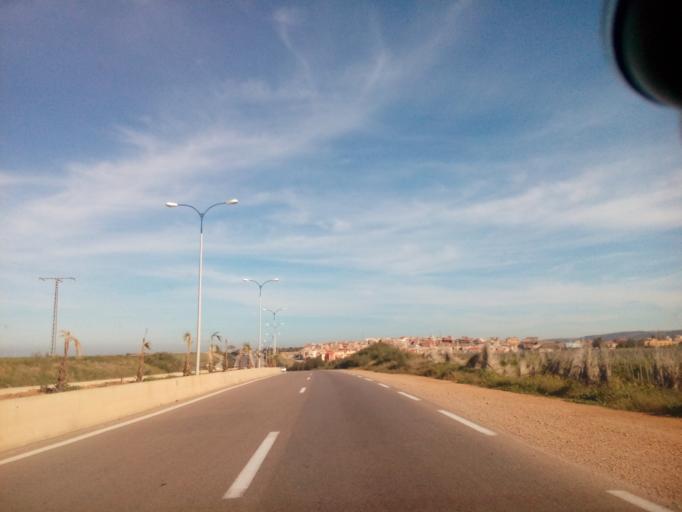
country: DZ
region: Mostaganem
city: Mostaganem
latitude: 35.8256
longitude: -0.0125
